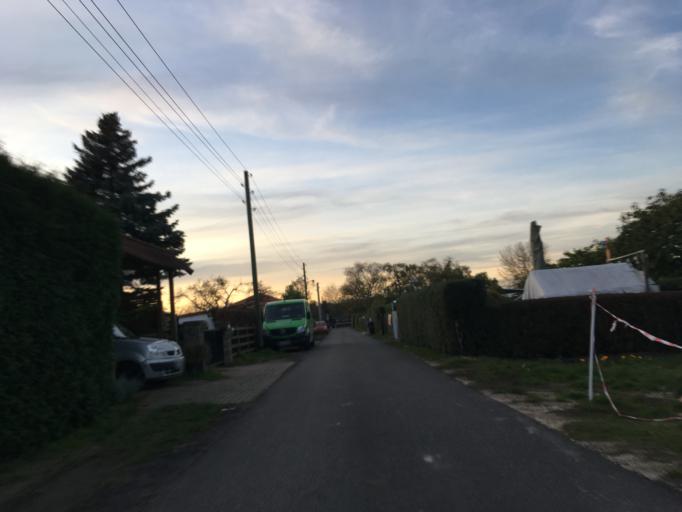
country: DE
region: Berlin
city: Buchholz
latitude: 52.6197
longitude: 13.4212
